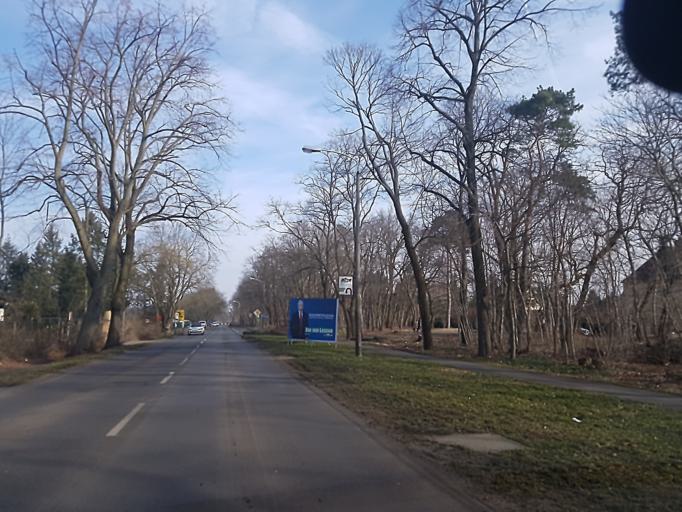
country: DE
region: Brandenburg
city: Brandenburg an der Havel
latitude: 52.3800
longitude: 12.5203
